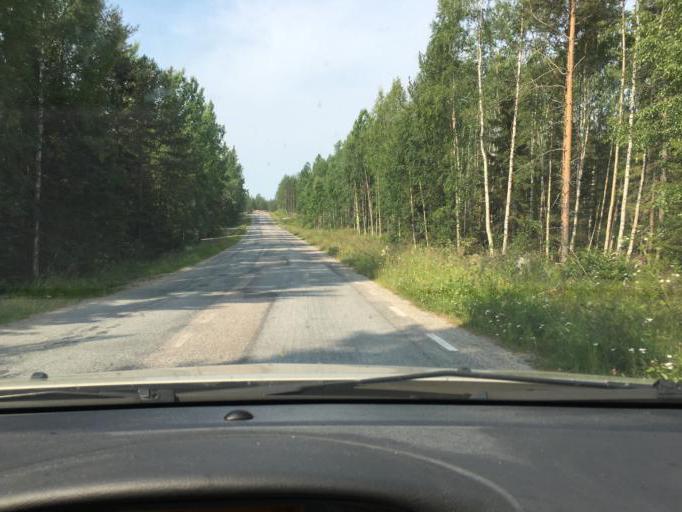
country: SE
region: Norrbotten
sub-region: Kalix Kommun
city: Rolfs
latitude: 65.7790
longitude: 22.9414
